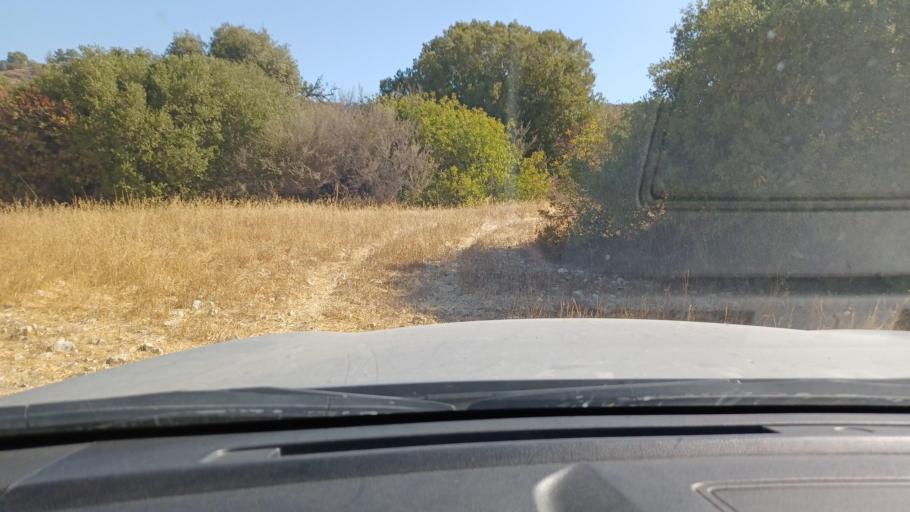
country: CY
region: Pafos
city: Polis
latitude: 34.9990
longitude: 32.5009
